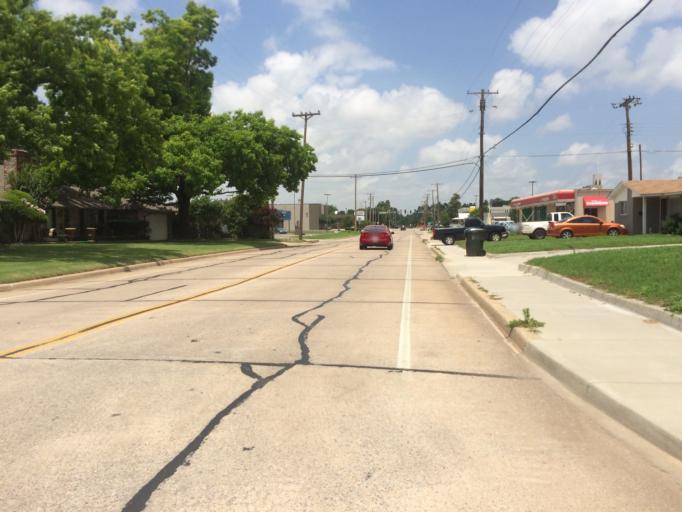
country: US
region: Oklahoma
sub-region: Cleveland County
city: Norman
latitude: 35.2016
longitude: -97.4678
